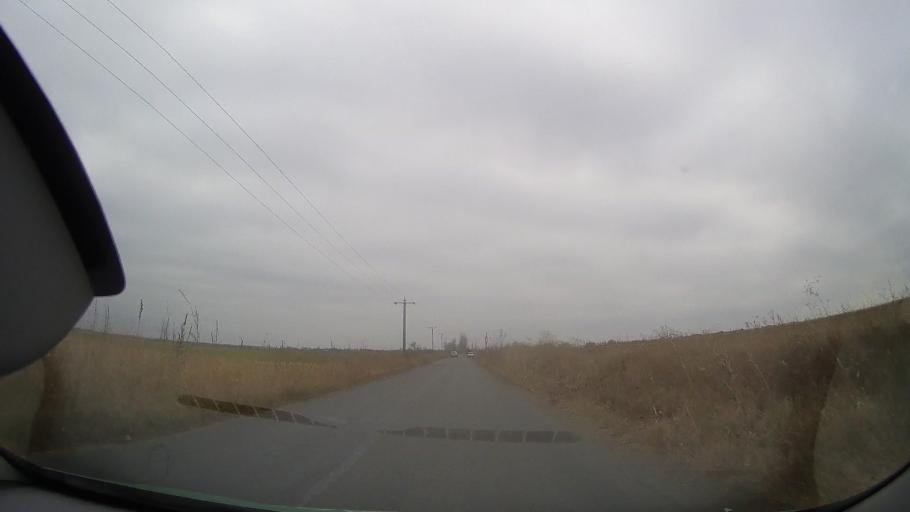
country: RO
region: Buzau
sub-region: Comuna Pogoanele
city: Pogoanele
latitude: 44.9406
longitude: 27.0056
